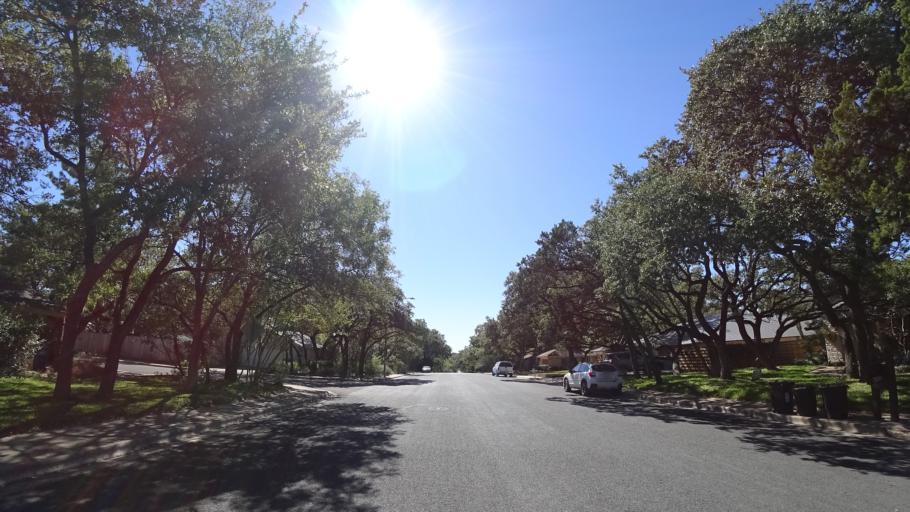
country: US
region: Texas
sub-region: Williamson County
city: Jollyville
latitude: 30.3647
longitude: -97.7553
